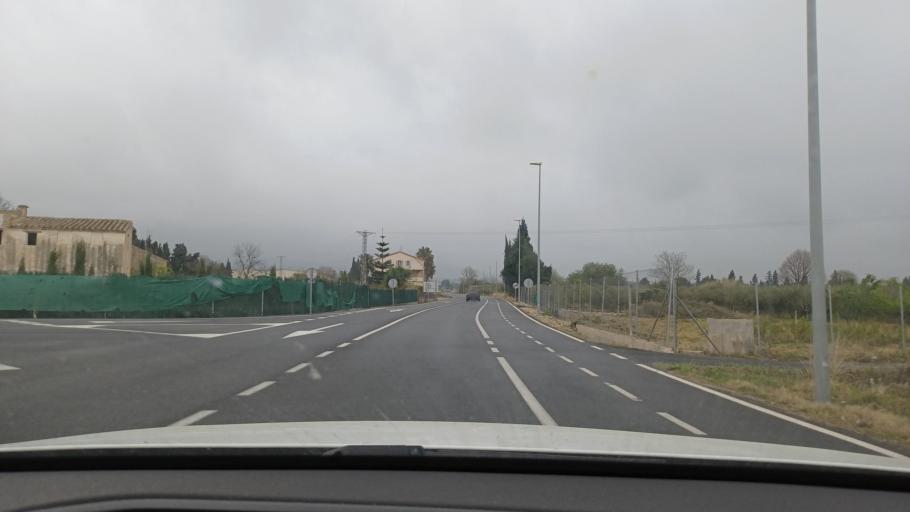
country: ES
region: Catalonia
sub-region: Provincia de Tarragona
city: Tortosa
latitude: 40.8087
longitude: 0.4998
